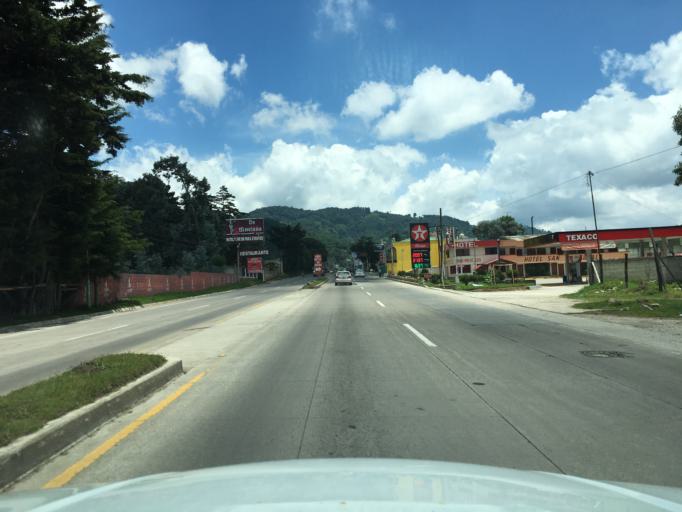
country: GT
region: Chimaltenango
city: Tecpan Guatemala
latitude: 14.7723
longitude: -90.9885
